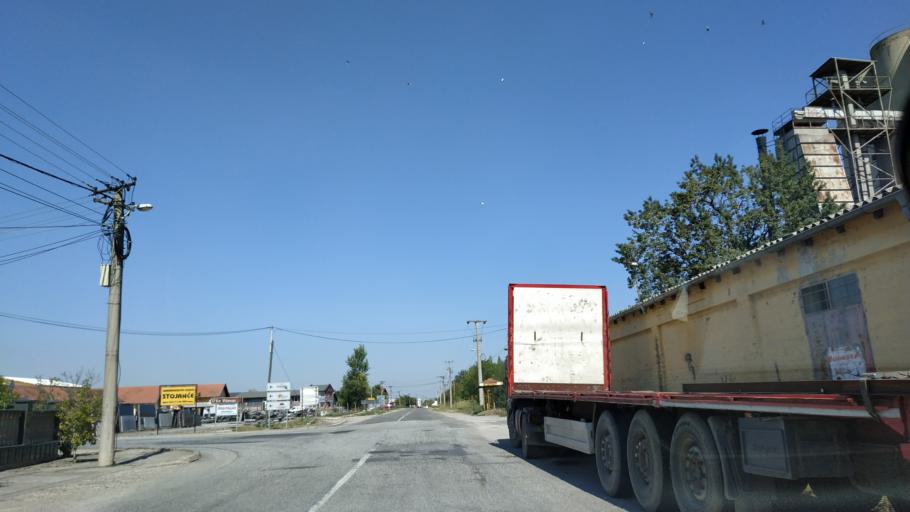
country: RS
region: Central Serbia
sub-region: Sumadijski Okrug
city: Lapovo
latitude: 44.2358
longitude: 21.0950
